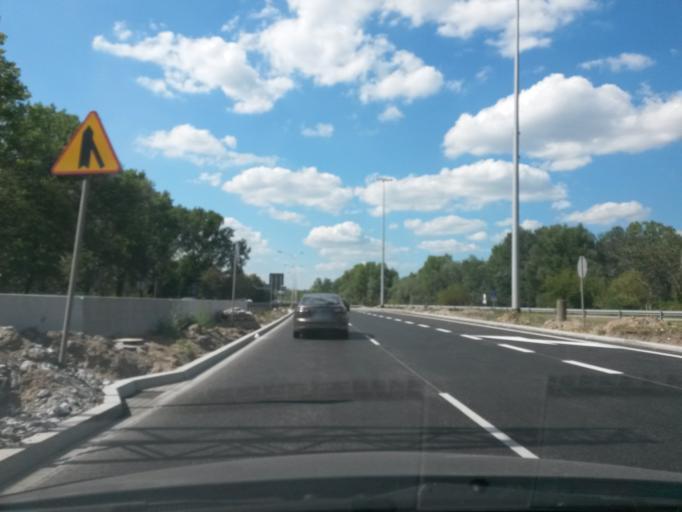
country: PL
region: Masovian Voivodeship
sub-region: Warszawa
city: Zoliborz
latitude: 52.2854
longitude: 20.9871
